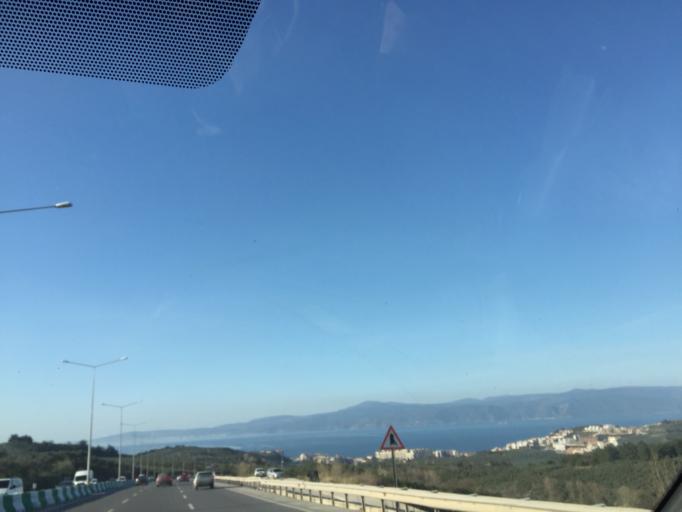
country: TR
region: Bursa
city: Niluefer
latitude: 40.3283
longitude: 28.9267
